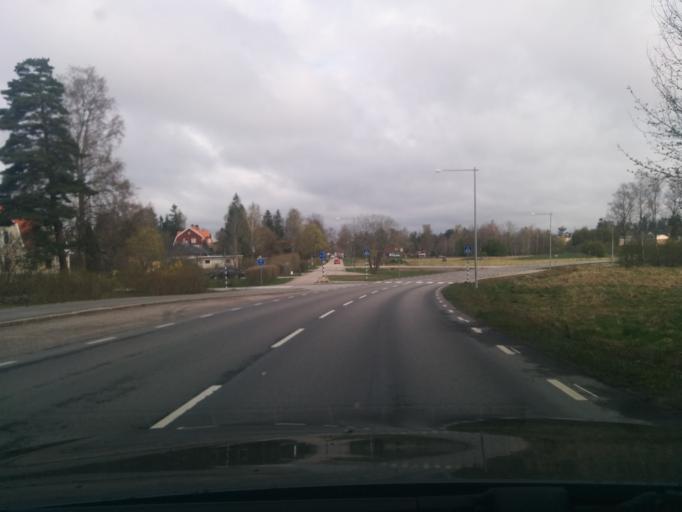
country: SE
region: Uppsala
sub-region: Tierps Kommun
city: Orbyhus
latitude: 60.2205
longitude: 17.7028
